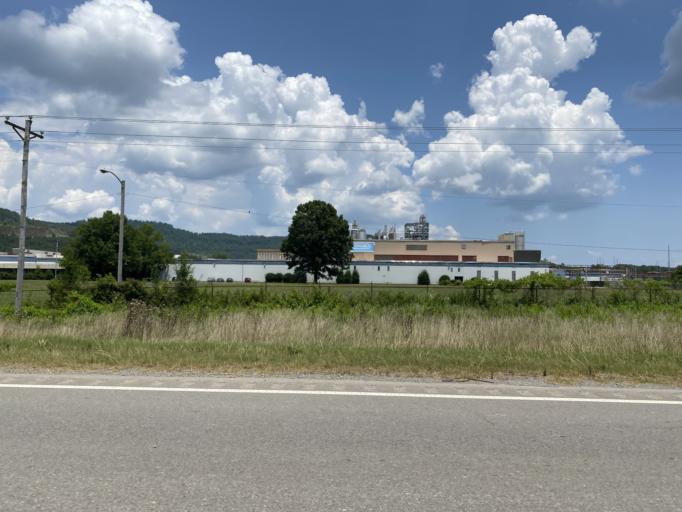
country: US
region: Alabama
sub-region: Jackson County
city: Scottsboro
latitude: 34.6166
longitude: -86.0861
